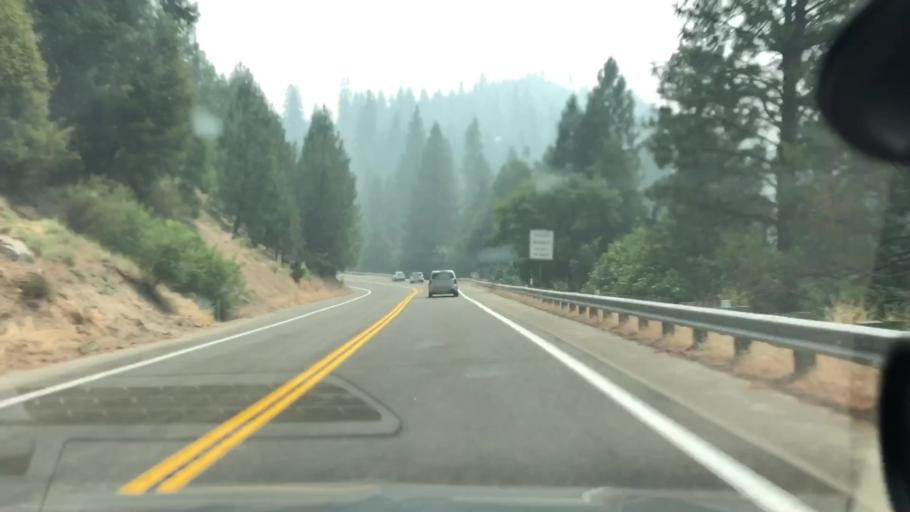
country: US
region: California
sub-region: El Dorado County
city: Pollock Pines
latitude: 38.7677
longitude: -120.3813
